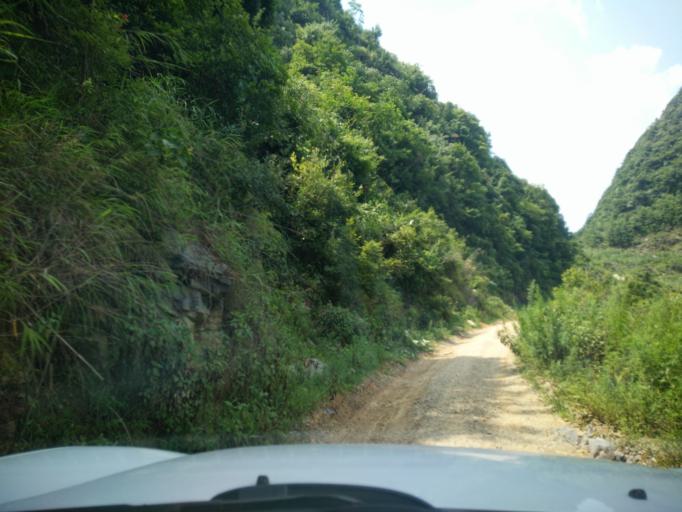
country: CN
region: Guangxi Zhuangzu Zizhiqu
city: Xinzhou
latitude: 25.0192
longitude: 105.7059
